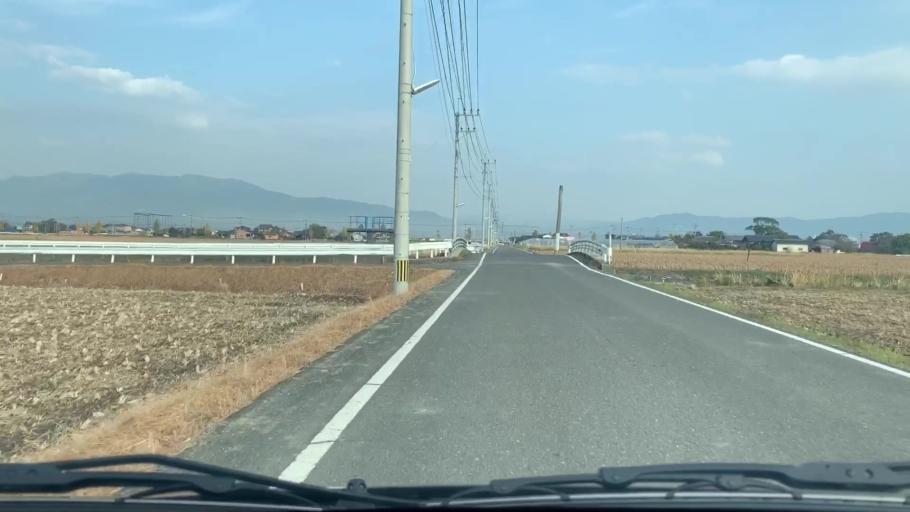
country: JP
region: Saga Prefecture
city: Saga-shi
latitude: 33.2505
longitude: 130.2581
